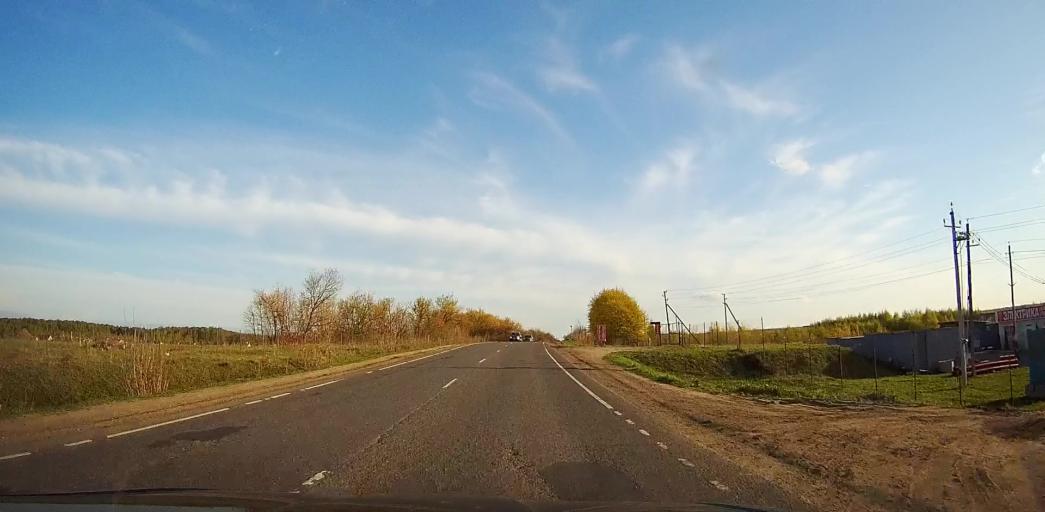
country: RU
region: Moskovskaya
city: Bronnitsy
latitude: 55.3240
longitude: 38.2192
